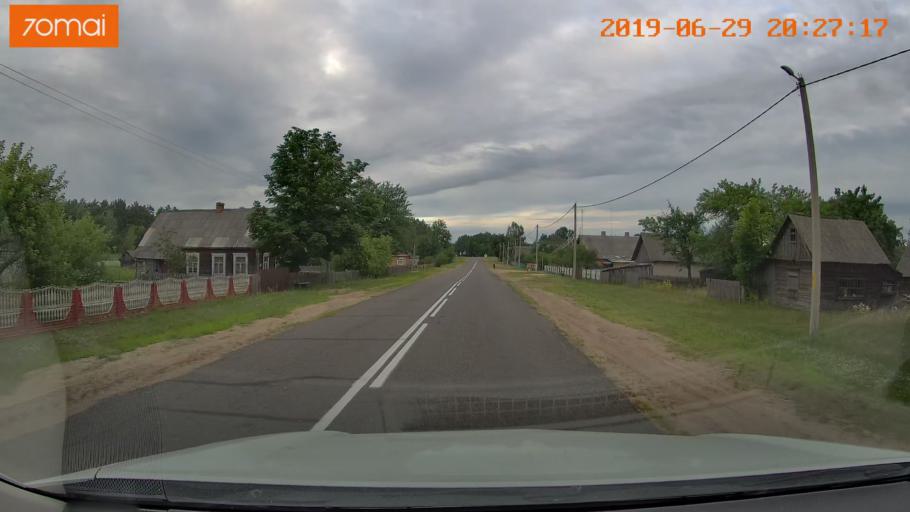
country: BY
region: Brest
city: Hantsavichy
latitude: 52.4727
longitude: 26.3031
